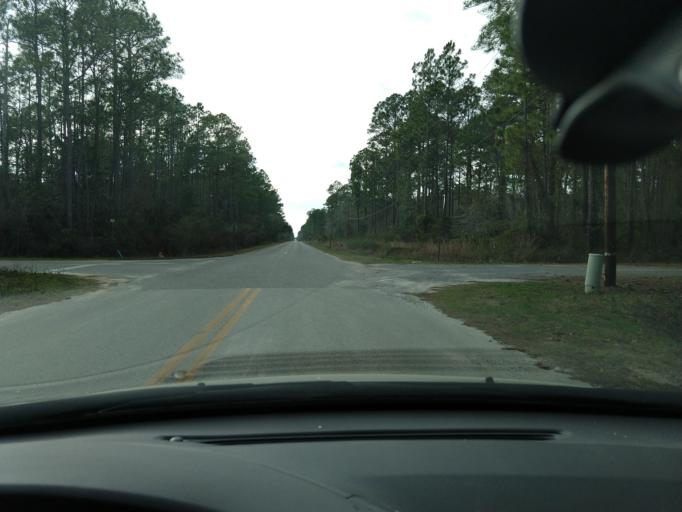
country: US
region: Florida
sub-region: Walton County
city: Seaside
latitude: 30.4031
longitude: -86.2113
